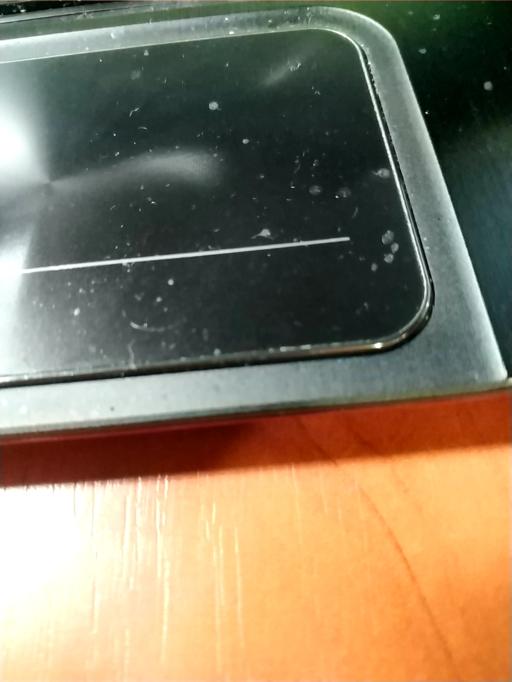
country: RU
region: Rjazan
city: Skopin
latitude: 53.9423
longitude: 39.5170
